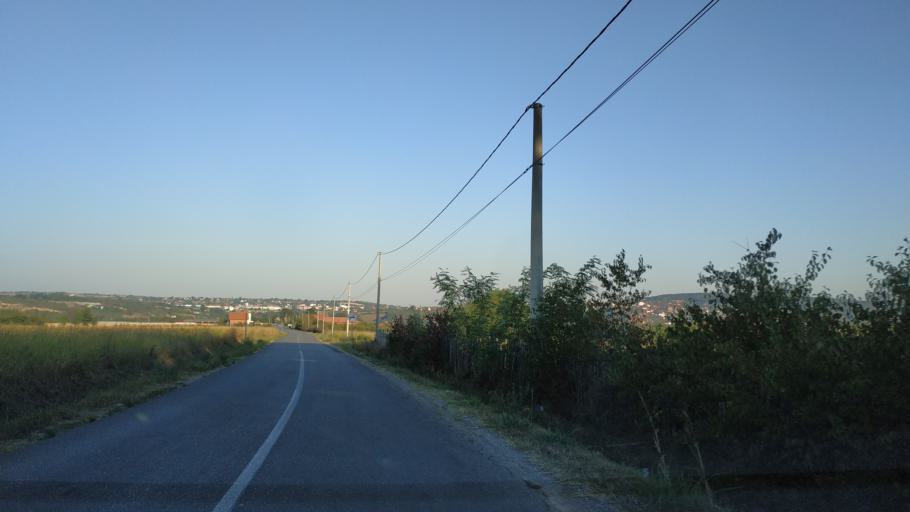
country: RS
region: Central Serbia
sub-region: Sumadijski Okrug
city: Topola
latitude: 44.2685
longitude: 20.6559
